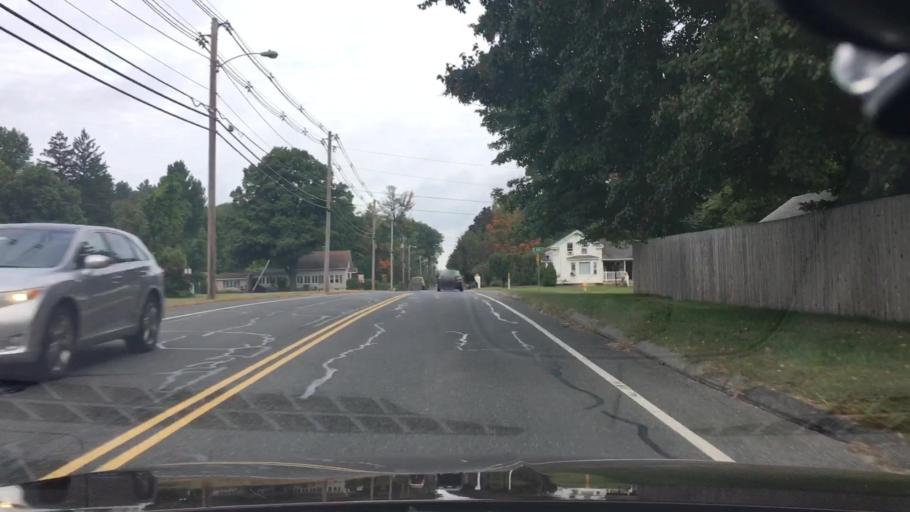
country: US
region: Massachusetts
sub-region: Hampden County
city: East Longmeadow
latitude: 42.0567
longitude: -72.5009
